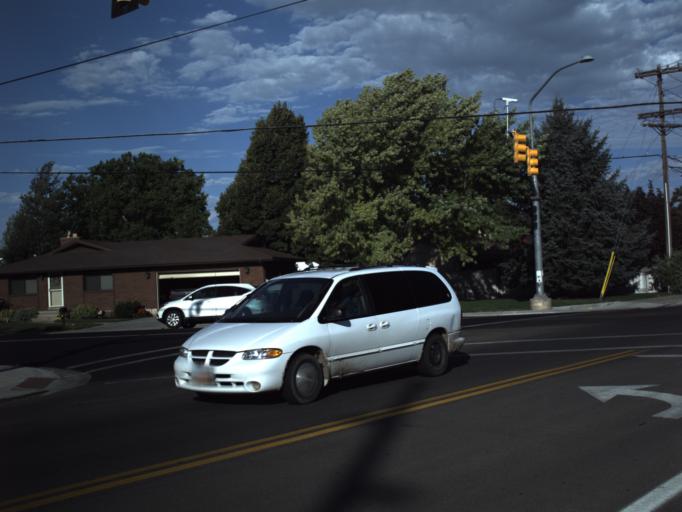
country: US
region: Utah
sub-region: Utah County
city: Spanish Fork
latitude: 40.1015
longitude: -111.6354
